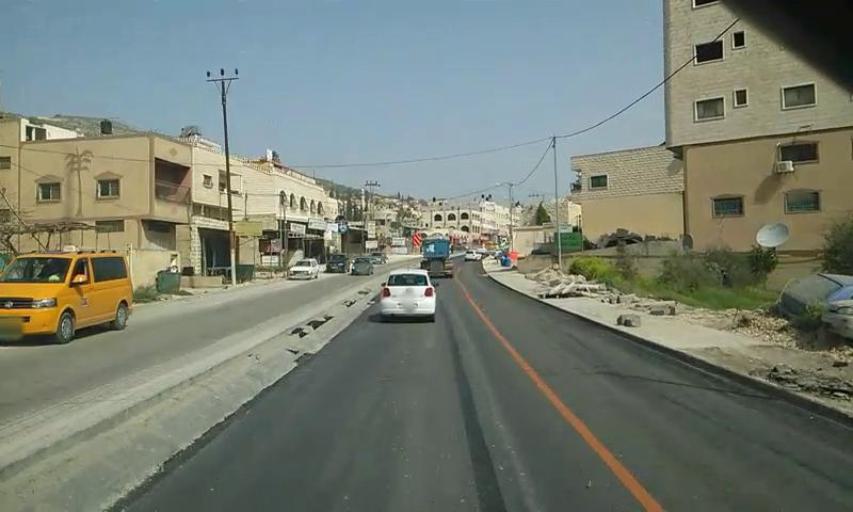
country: PS
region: West Bank
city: Huwwarah
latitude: 32.1475
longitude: 35.2578
